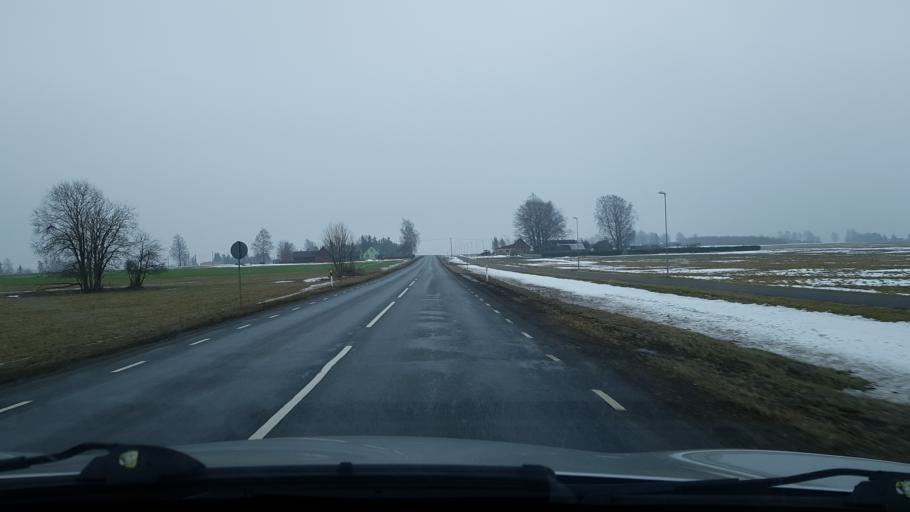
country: EE
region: Valgamaa
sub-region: Torva linn
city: Torva
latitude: 58.2248
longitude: 25.8903
